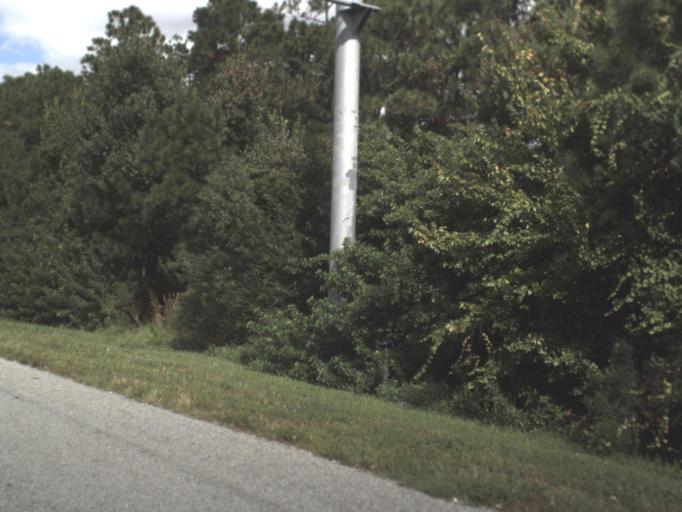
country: US
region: Florida
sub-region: Orange County
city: Oak Ridge
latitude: 28.4524
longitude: -81.4223
